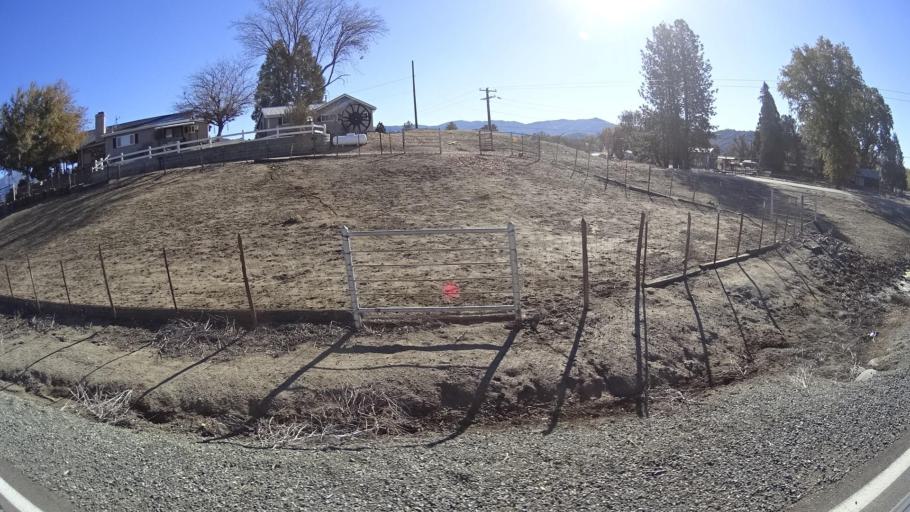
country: US
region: California
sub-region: Kern County
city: Alta Sierra
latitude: 35.7242
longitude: -118.7229
